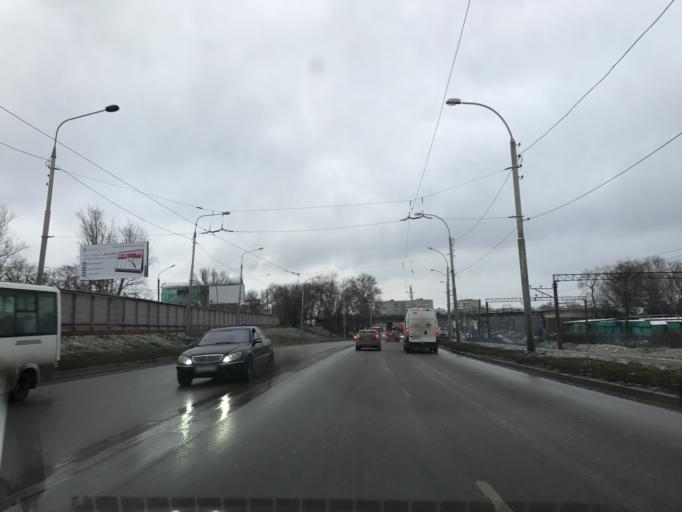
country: RU
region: Rostov
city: Imeni Chkalova
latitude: 47.2615
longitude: 39.7697
